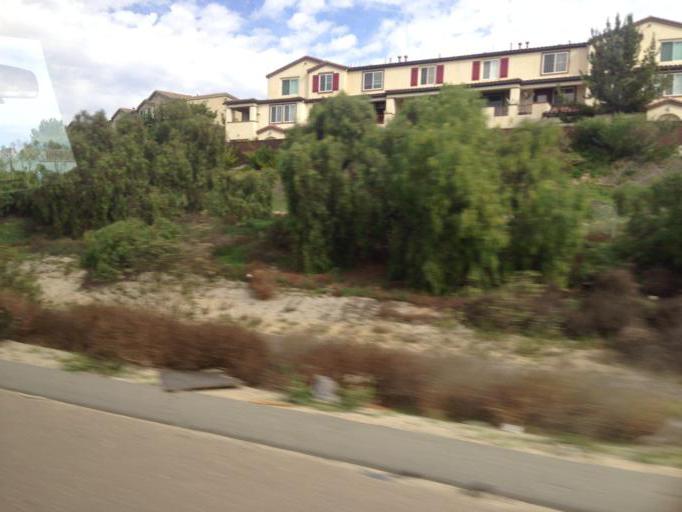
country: US
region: California
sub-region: San Diego County
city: Imperial Beach
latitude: 32.5715
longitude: -117.0392
